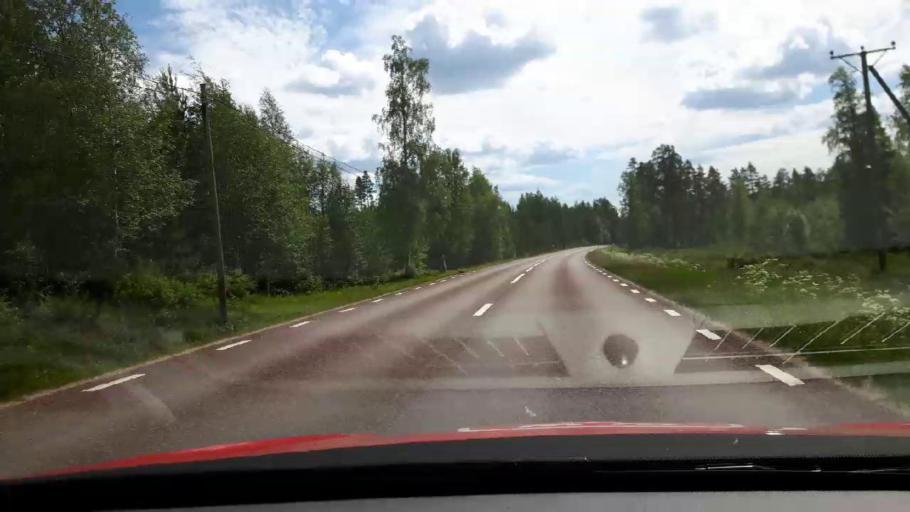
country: SE
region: Jaemtland
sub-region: Harjedalens Kommun
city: Sveg
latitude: 62.1383
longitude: 14.9662
